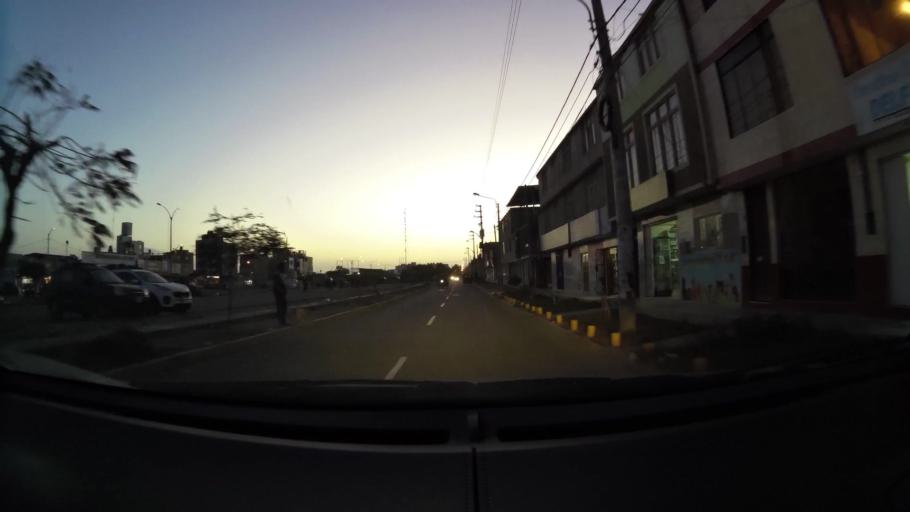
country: PE
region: Ancash
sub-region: Provincia de Santa
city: Buenos Aires
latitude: -9.1265
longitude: -78.5197
